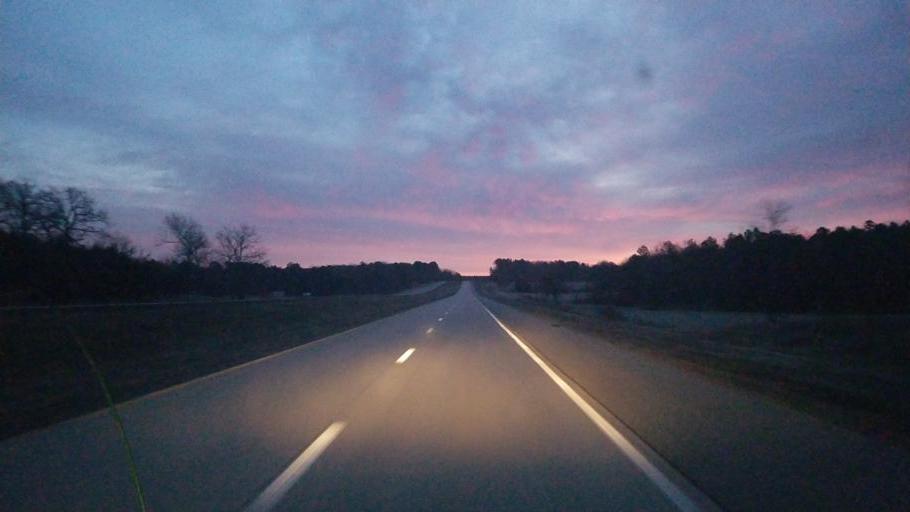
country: US
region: Missouri
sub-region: Shannon County
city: Winona
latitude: 36.9982
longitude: -91.4361
